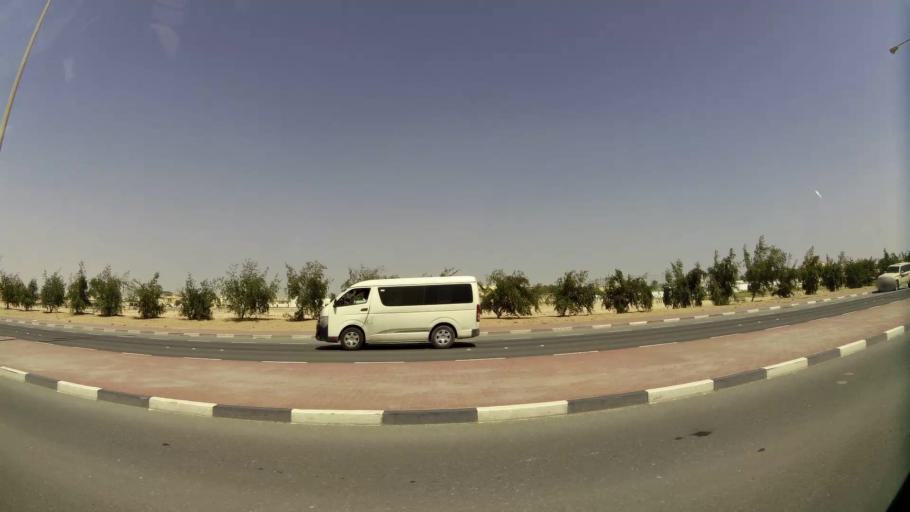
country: QA
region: Baladiyat Umm Salal
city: Umm Salal Muhammad
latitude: 25.3872
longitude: 51.4235
